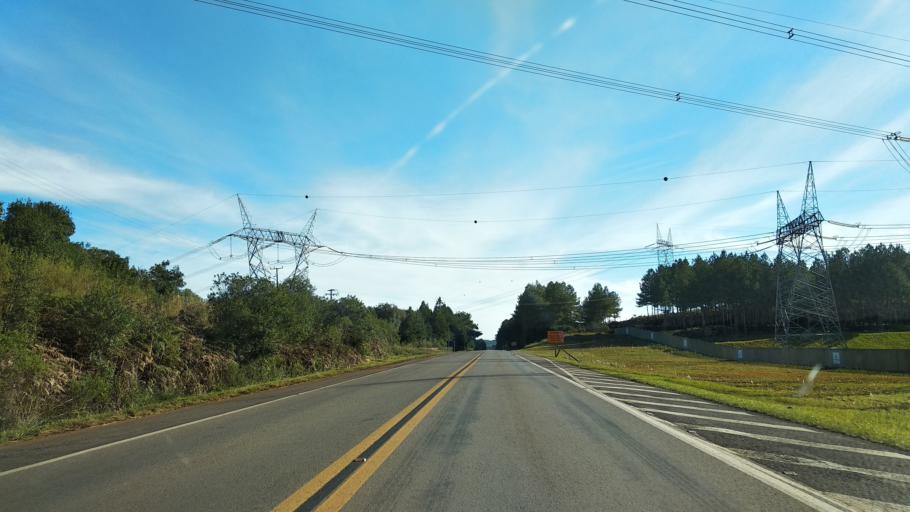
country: BR
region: Santa Catarina
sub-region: Celso Ramos
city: Celso Ramos
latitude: -27.5416
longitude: -51.4169
